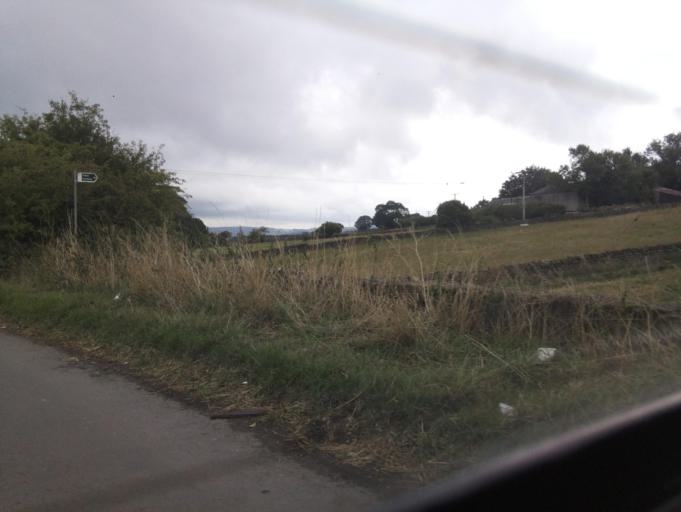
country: GB
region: England
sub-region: Kirklees
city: Shelley
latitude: 53.5994
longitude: -1.6810
